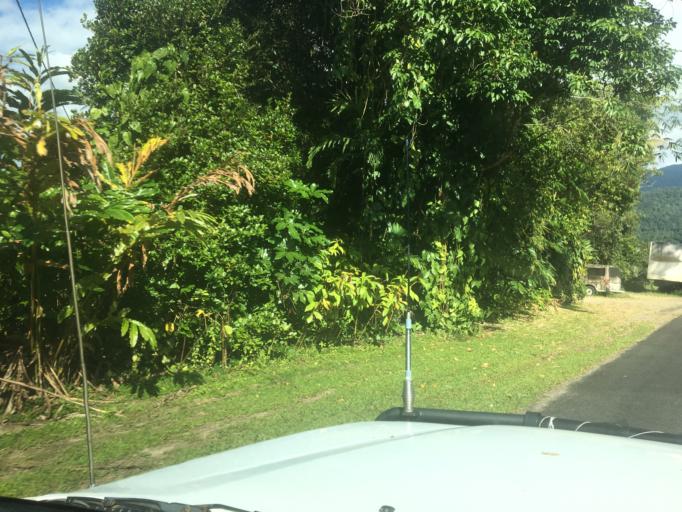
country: AU
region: Queensland
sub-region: Cassowary Coast
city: Innisfail
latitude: -17.3476
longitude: 145.8836
